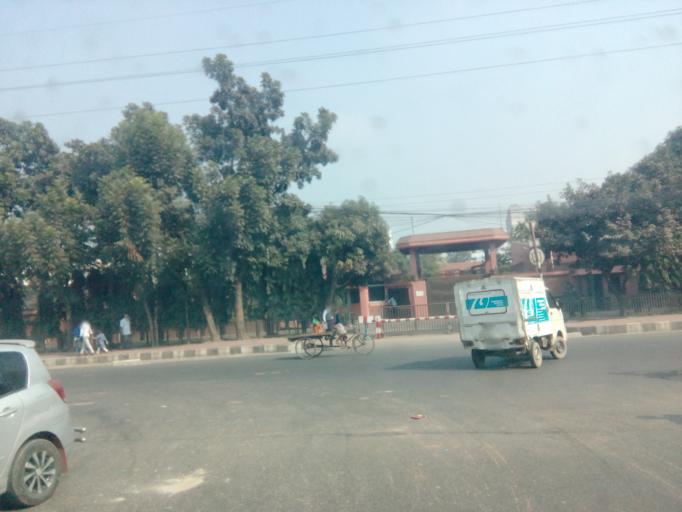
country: BD
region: Dhaka
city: Paltan
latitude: 23.7957
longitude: 90.4241
